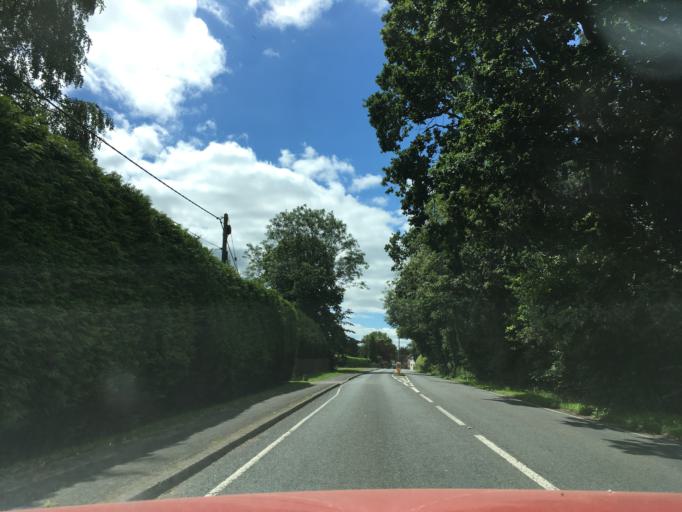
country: GB
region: England
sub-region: Hampshire
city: Highclere
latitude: 51.3405
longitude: -1.3743
